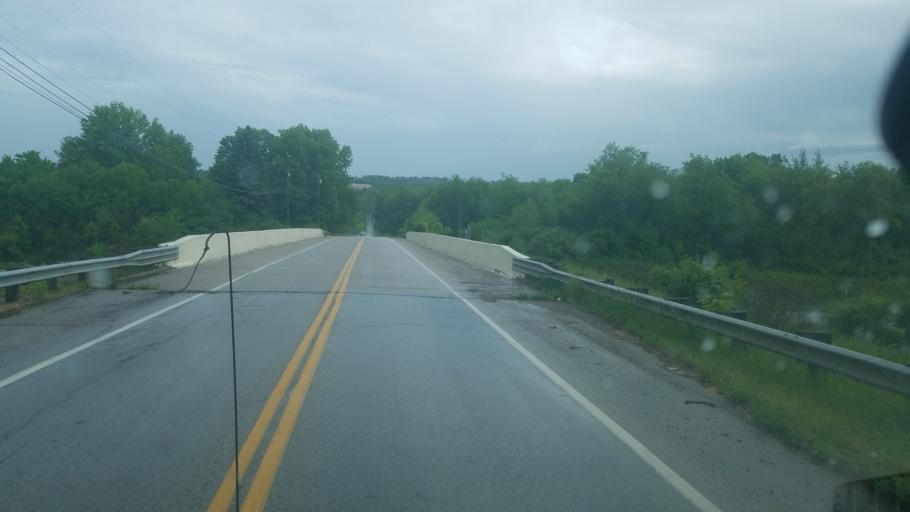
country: US
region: Ohio
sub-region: Wayne County
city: Wooster
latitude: 40.7987
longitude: -81.9055
